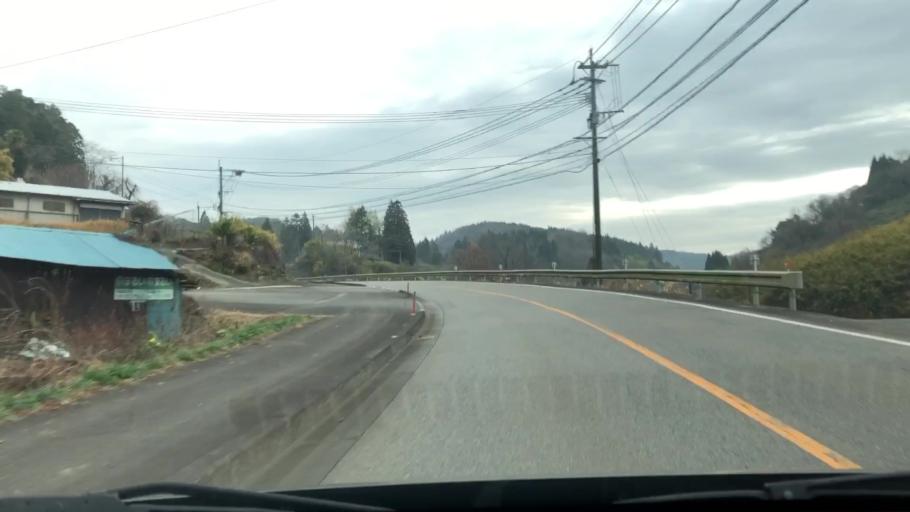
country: JP
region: Oita
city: Usuki
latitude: 33.0084
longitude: 131.6429
